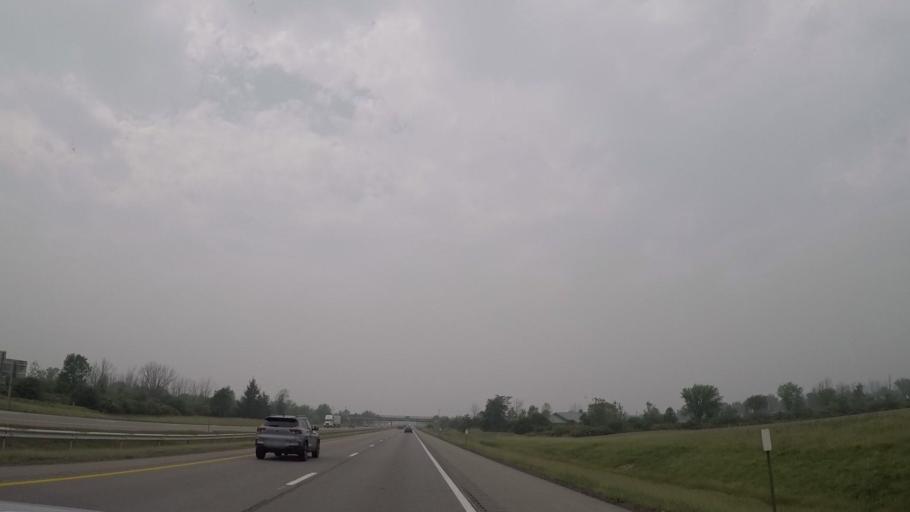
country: US
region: New York
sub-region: Erie County
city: Grandyle Village
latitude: 43.0333
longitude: -78.9821
